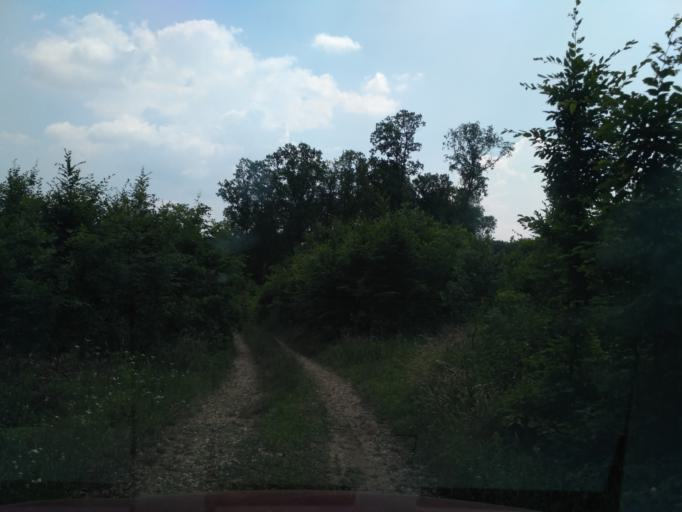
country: SK
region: Kosicky
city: Moldava nad Bodvou
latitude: 48.6559
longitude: 21.0440
